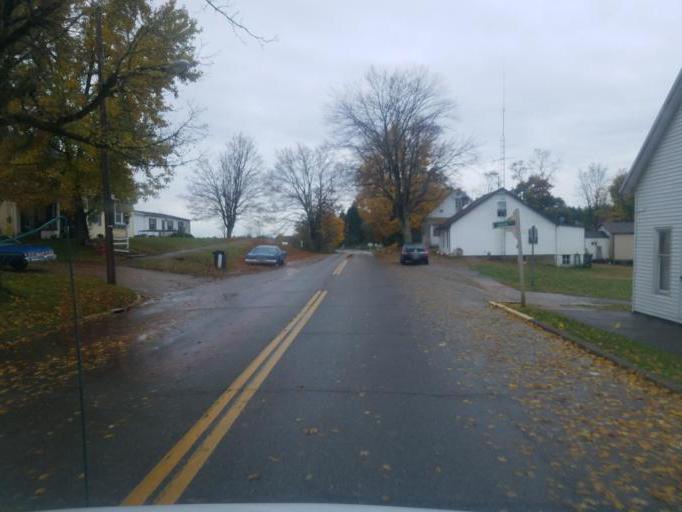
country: US
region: Ohio
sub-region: Morgan County
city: McConnelsville
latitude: 39.4865
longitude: -81.8673
